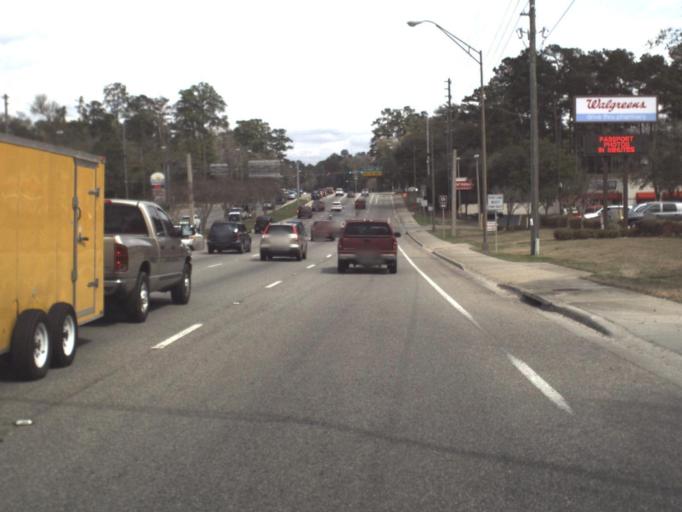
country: US
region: Florida
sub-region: Leon County
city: Tallahassee
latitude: 30.5105
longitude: -84.2466
